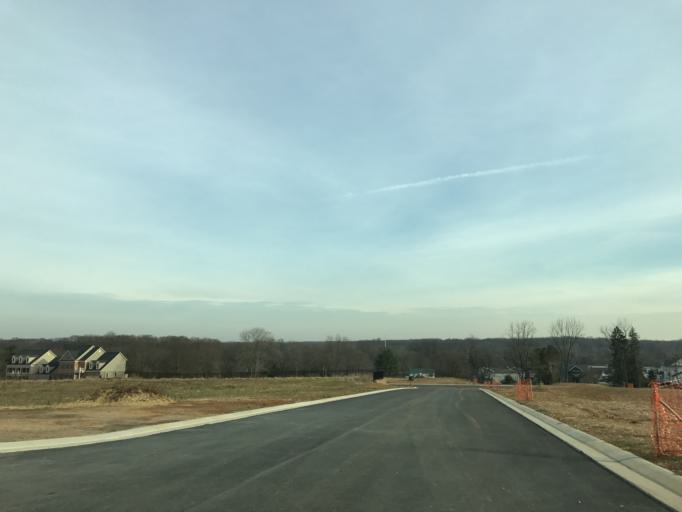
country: US
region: Maryland
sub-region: Baltimore County
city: White Marsh
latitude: 39.3868
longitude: -76.4336
